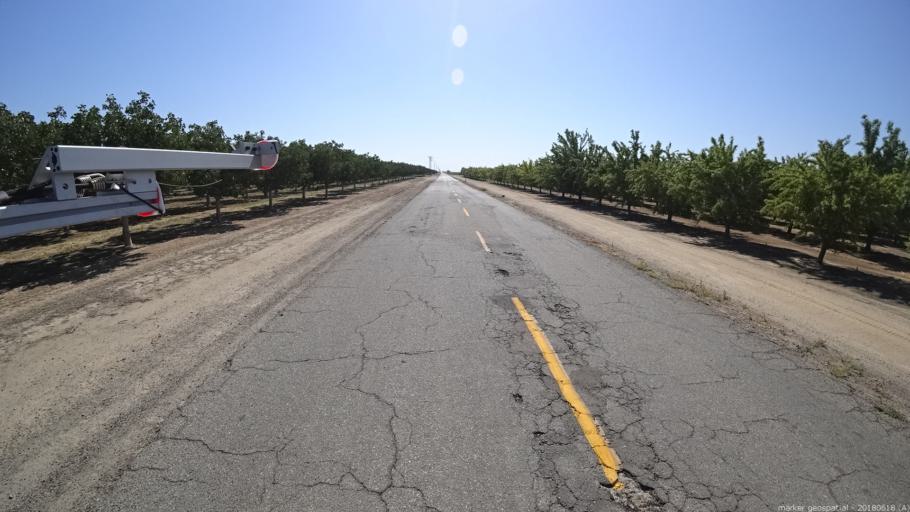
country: US
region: California
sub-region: Fresno County
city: Mendota
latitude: 36.8366
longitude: -120.2260
